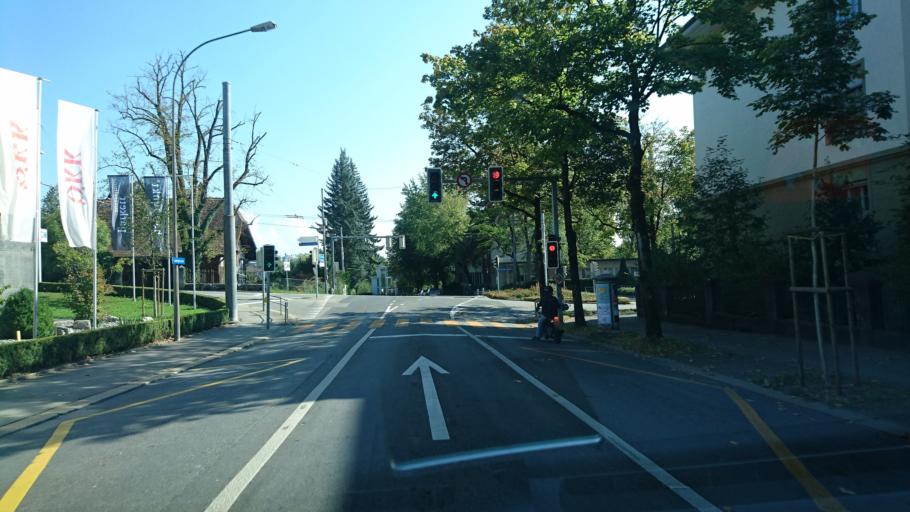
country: CH
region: Bern
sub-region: Bern-Mittelland District
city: Bern
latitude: 46.9479
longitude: 7.4658
